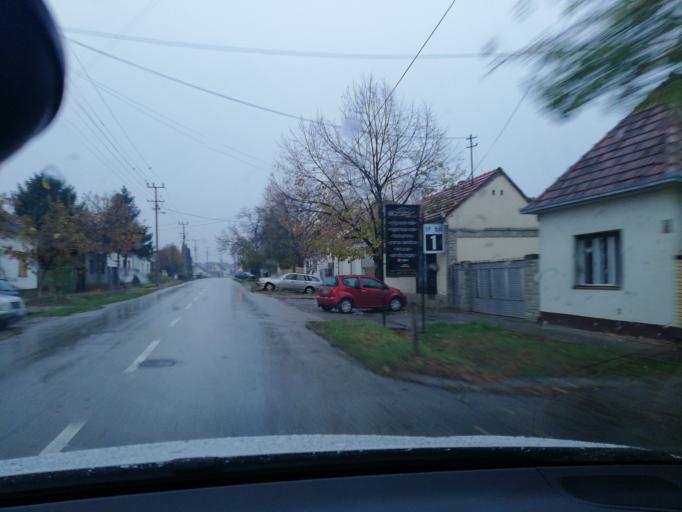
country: RS
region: Autonomna Pokrajina Vojvodina
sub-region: Sremski Okrug
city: Ruma
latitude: 45.0051
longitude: 19.8389
